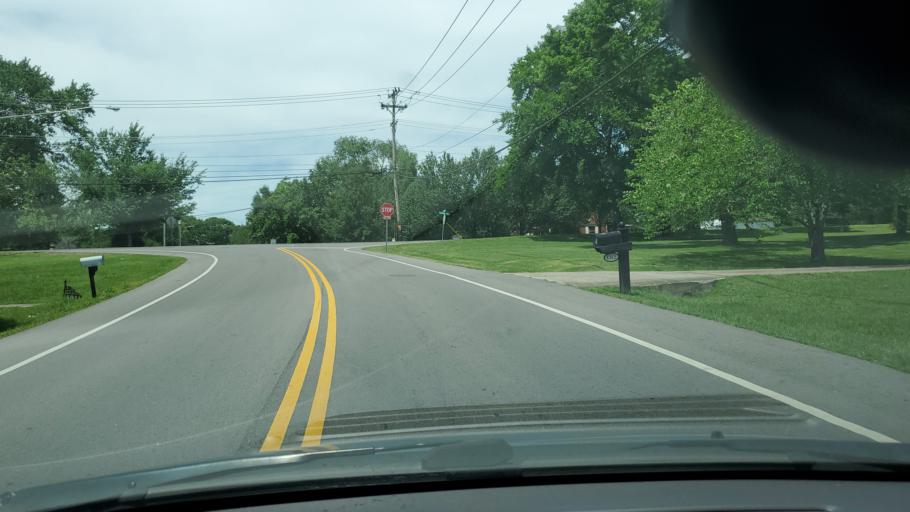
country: US
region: Tennessee
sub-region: Davidson County
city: Nashville
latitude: 36.2292
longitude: -86.7326
